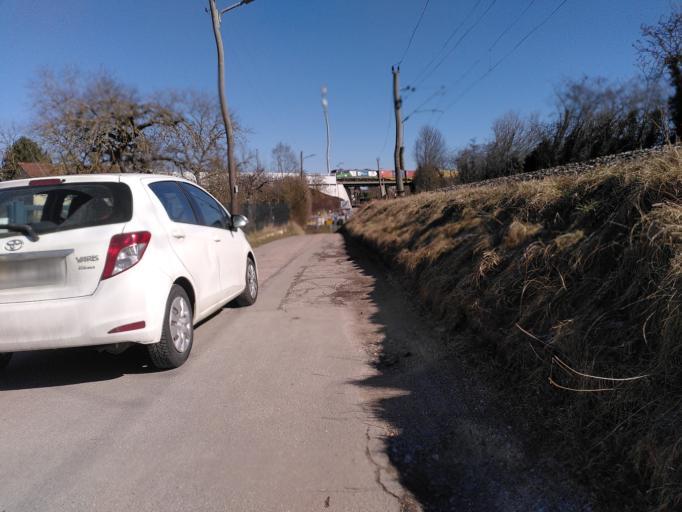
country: DE
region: Bavaria
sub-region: Upper Palatinate
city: Sinzing
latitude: 49.0102
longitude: 12.0381
